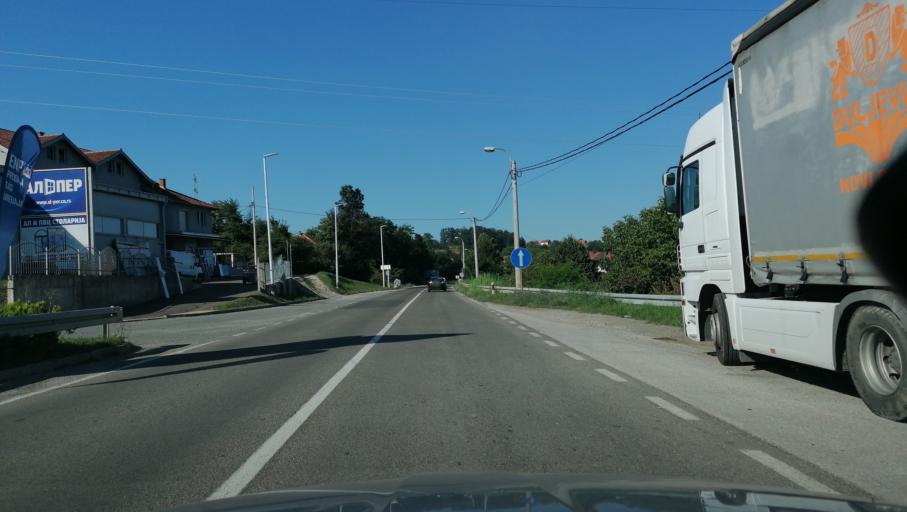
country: RS
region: Central Serbia
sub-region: Raski Okrug
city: Kraljevo
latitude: 43.7119
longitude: 20.6175
